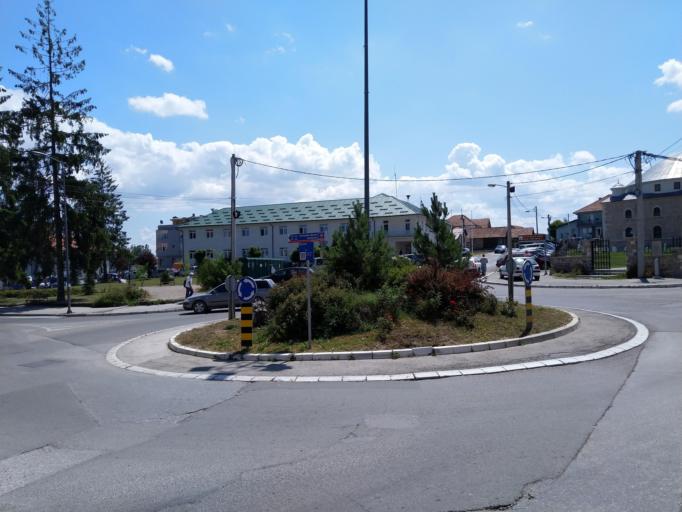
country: RS
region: Central Serbia
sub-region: Zlatiborski Okrug
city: Sjenica
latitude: 43.2727
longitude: 19.9984
